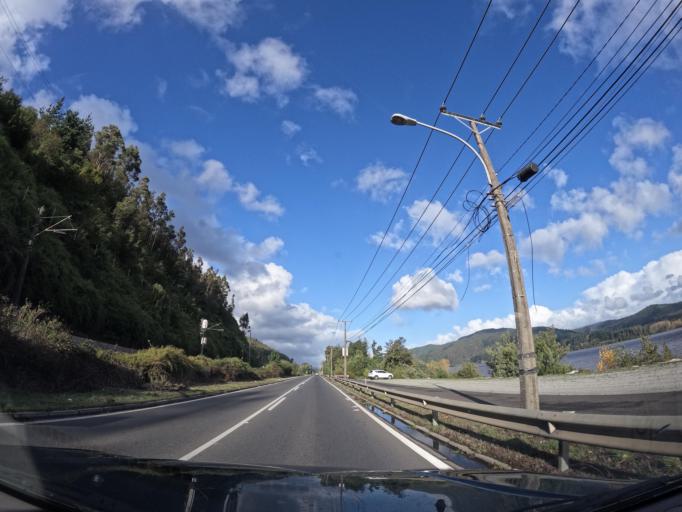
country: CL
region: Biobio
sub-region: Provincia de Concepcion
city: Chiguayante
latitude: -36.9652
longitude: -73.0061
